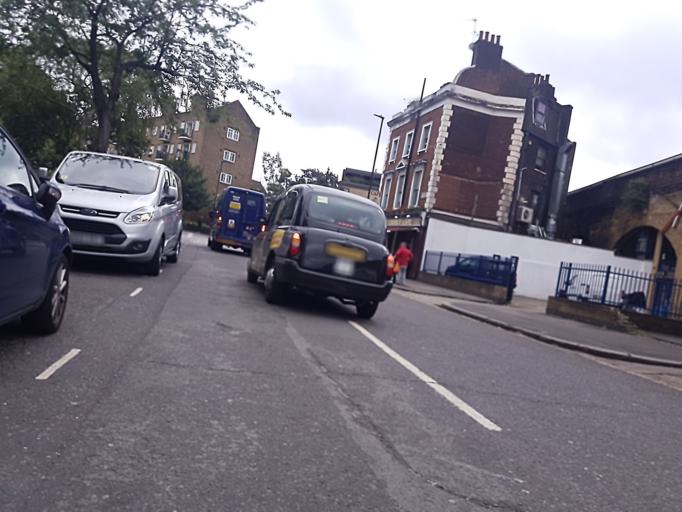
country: GB
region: England
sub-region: Greater London
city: Lambeth
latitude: 51.4962
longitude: -0.1150
